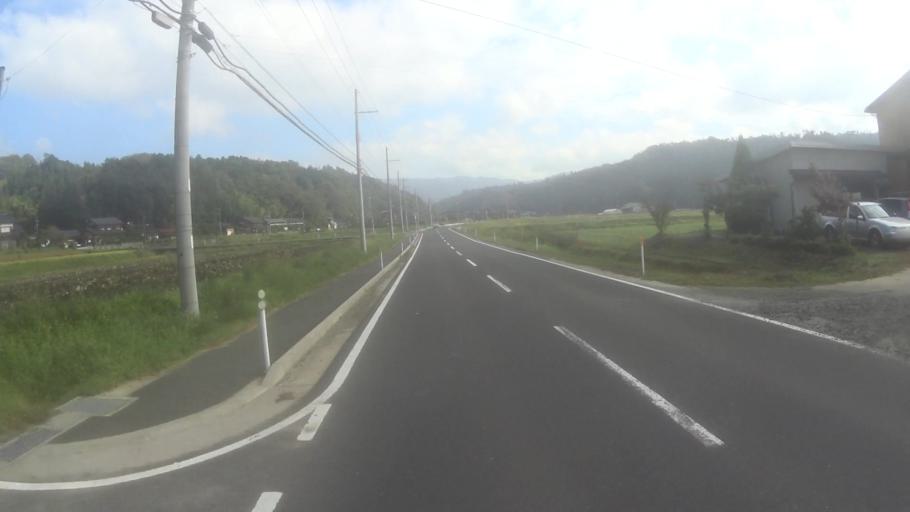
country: JP
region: Kyoto
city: Miyazu
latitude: 35.5795
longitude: 135.1240
